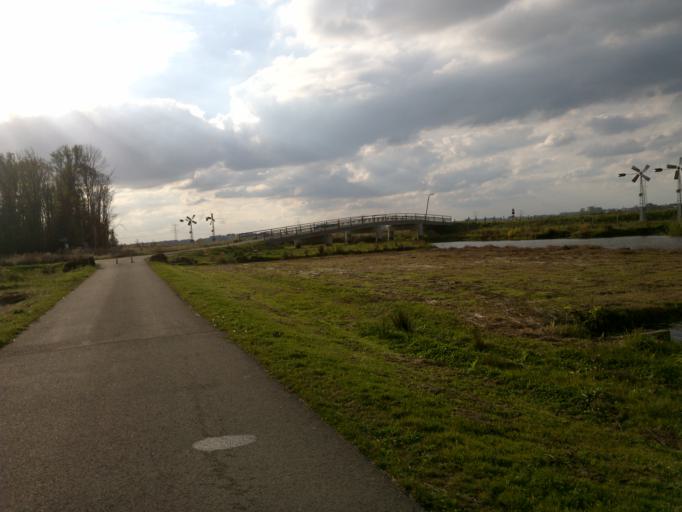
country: NL
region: South Holland
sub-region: Gemeente Hardinxveld-Giessendam
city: Neder-Hardinxveld
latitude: 51.7843
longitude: 4.8461
